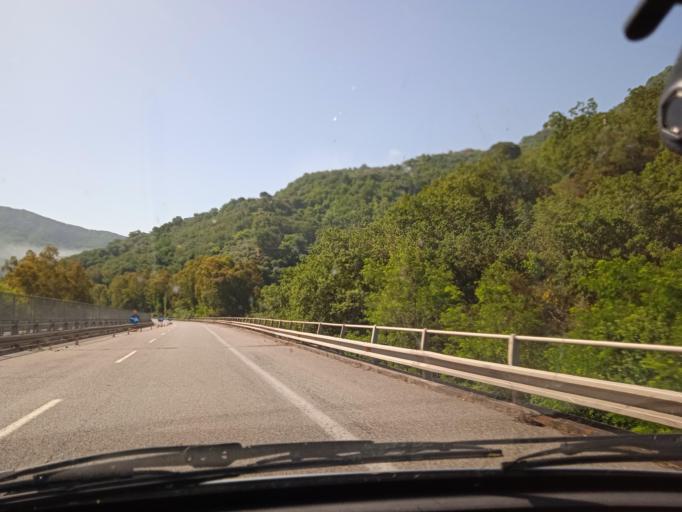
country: IT
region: Sicily
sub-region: Messina
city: Piraino
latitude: 38.1431
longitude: 14.8634
